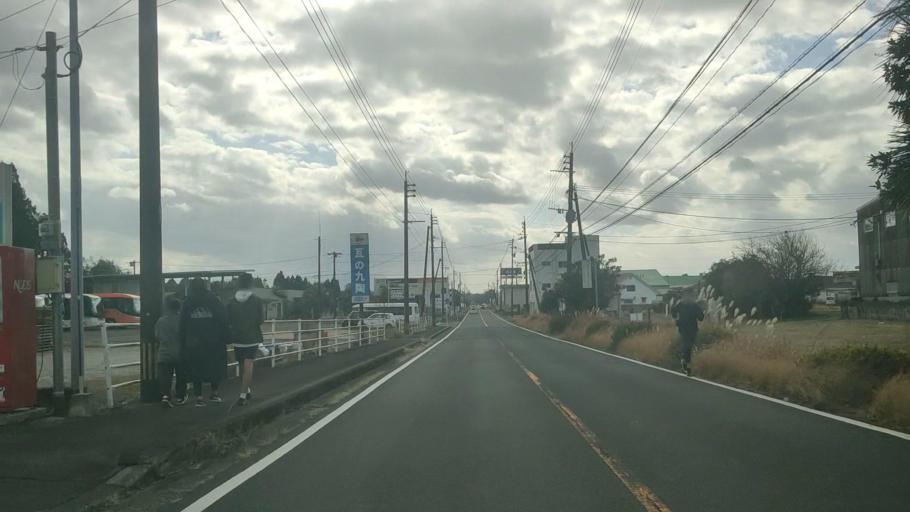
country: JP
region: Kagoshima
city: Kajiki
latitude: 31.7844
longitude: 130.7056
